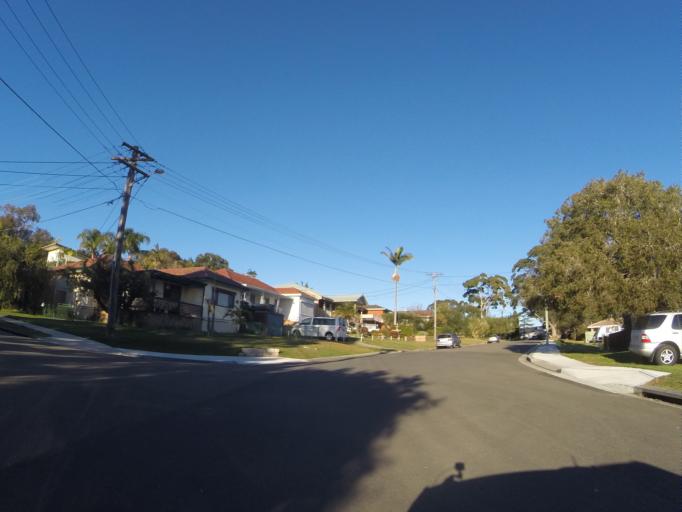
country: AU
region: New South Wales
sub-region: Sutherland Shire
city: Loftus
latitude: -34.0408
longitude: 151.0439
